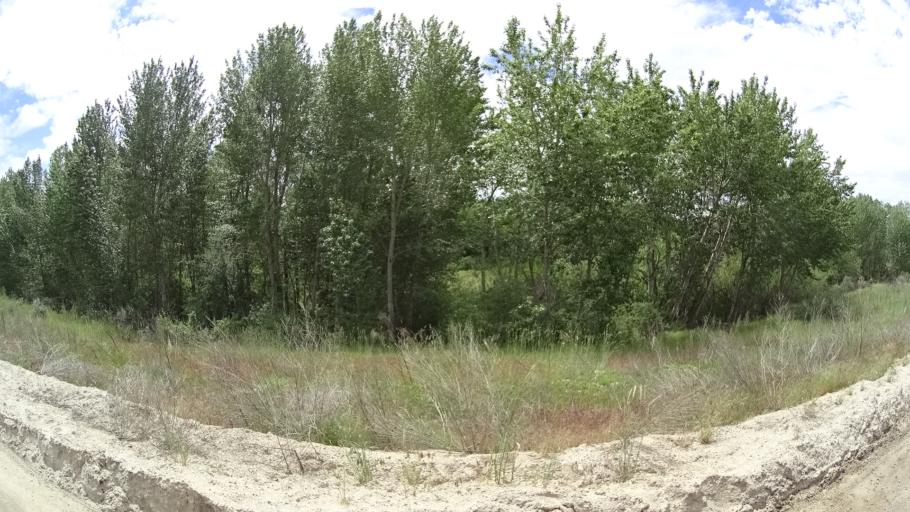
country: US
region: Idaho
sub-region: Ada County
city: Boise
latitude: 43.6411
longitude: -116.1920
